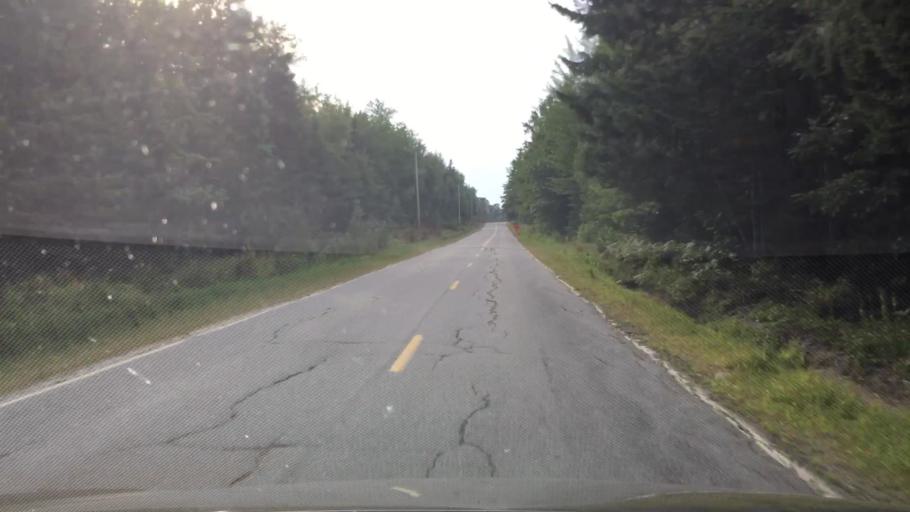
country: US
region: Maine
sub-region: Hancock County
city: Penobscot
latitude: 44.4732
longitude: -68.7701
